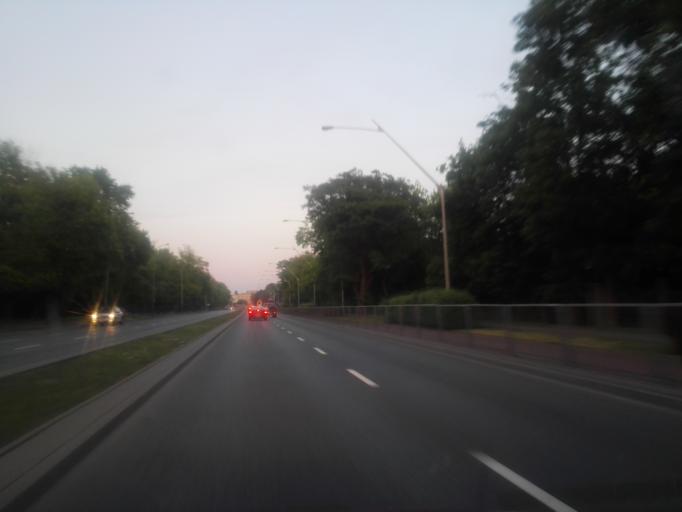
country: PL
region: Masovian Voivodeship
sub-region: Warszawa
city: Ochota
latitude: 52.1964
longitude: 20.9948
